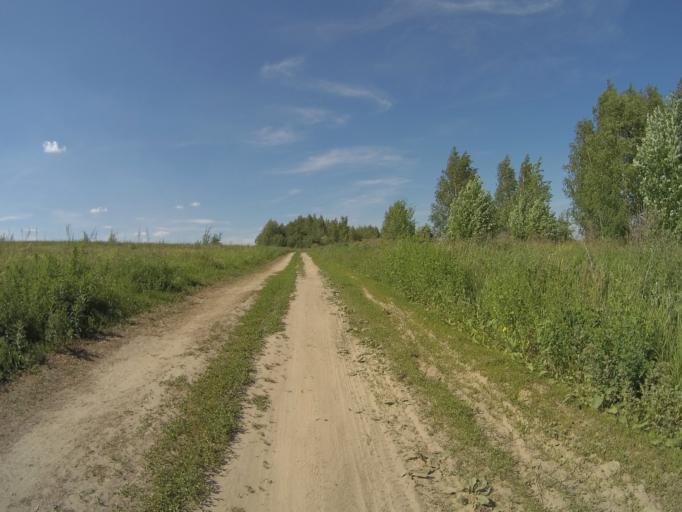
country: RU
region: Vladimir
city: Raduzhnyy
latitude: 55.9979
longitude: 40.3711
